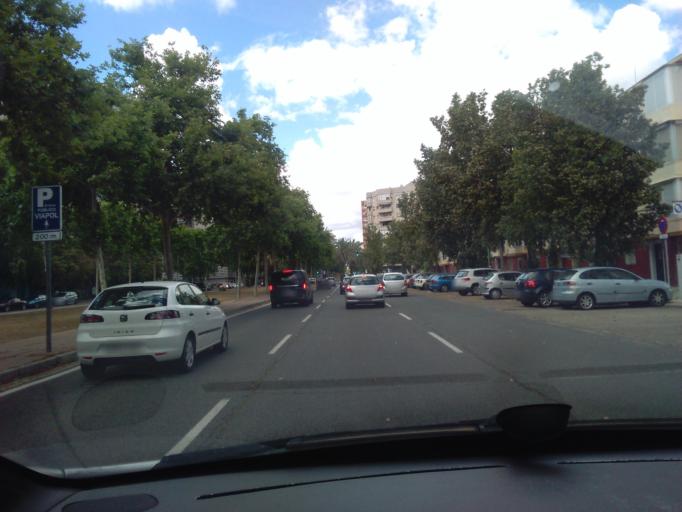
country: ES
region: Andalusia
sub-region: Provincia de Sevilla
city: Sevilla
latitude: 37.3731
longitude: -5.9763
